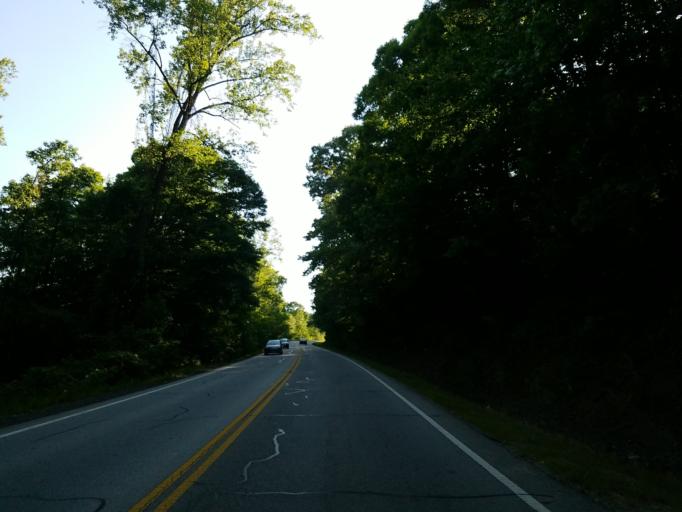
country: US
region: Georgia
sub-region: Paulding County
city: Dallas
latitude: 33.8580
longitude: -84.9250
